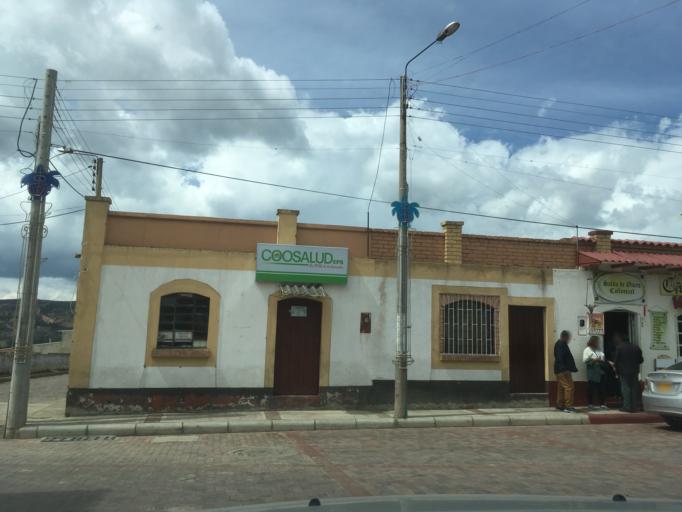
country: CO
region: Boyaca
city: Pesca
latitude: 5.5609
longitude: -72.9863
